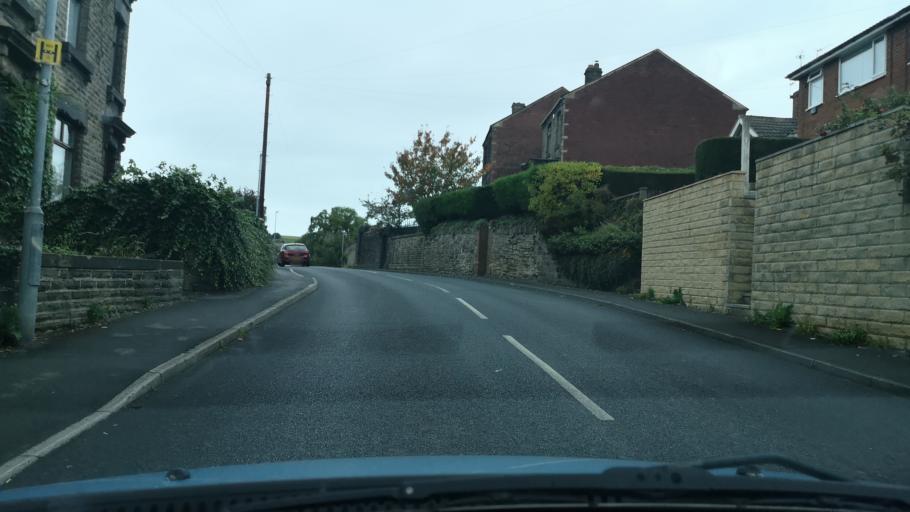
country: GB
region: England
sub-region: Kirklees
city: Heckmondwike
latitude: 53.7121
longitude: -1.6739
